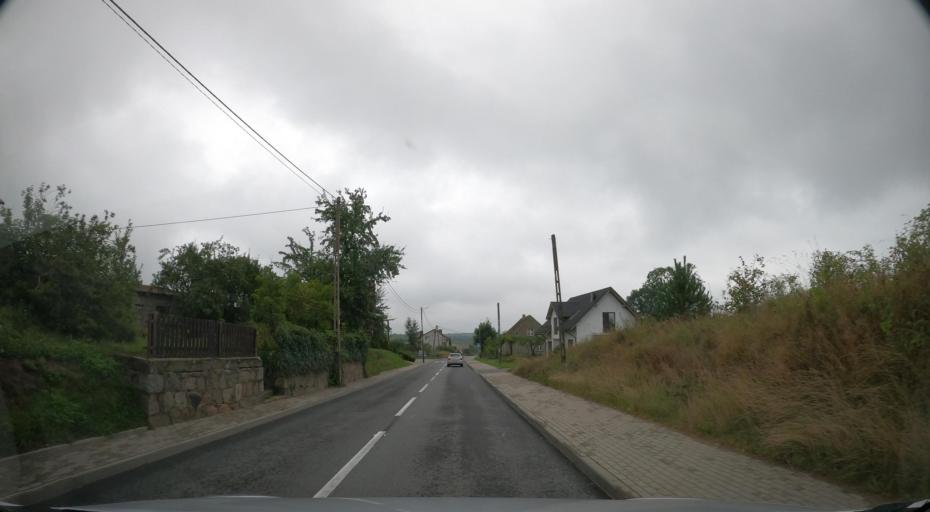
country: PL
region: Pomeranian Voivodeship
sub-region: Powiat wejherowski
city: Linia
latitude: 54.4820
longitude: 17.8524
